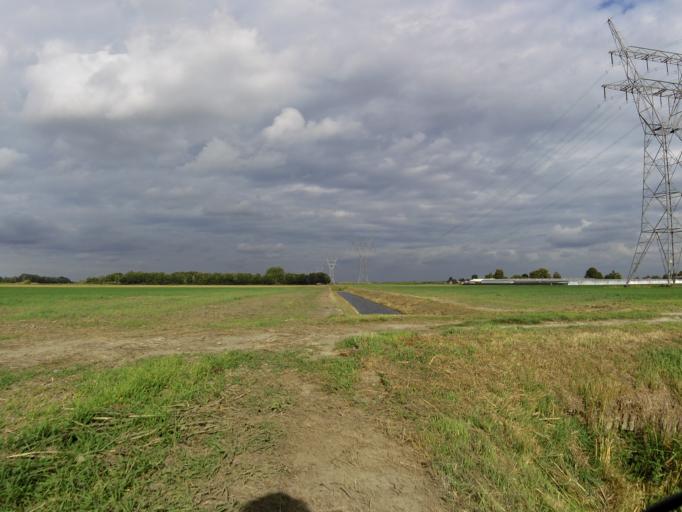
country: NL
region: South Holland
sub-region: Gemeente Rijnwoude
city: Benthuizen
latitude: 52.0504
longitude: 4.5694
